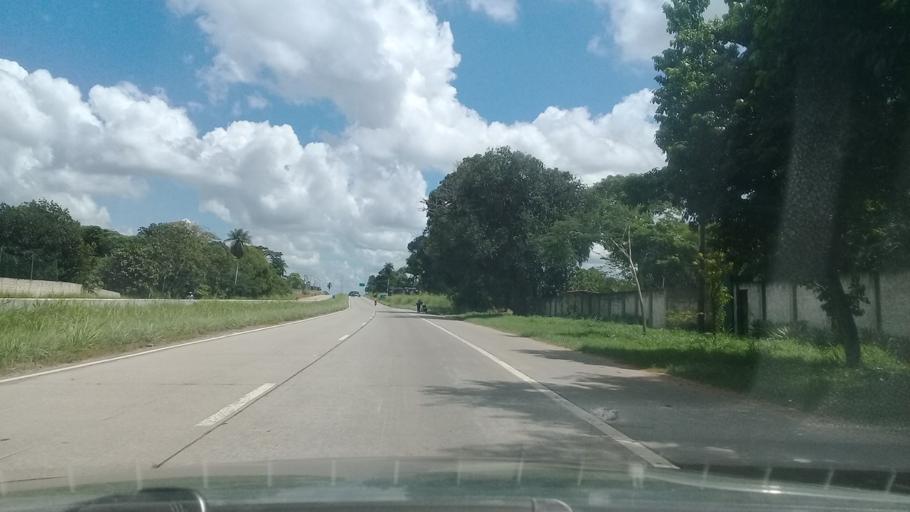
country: BR
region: Pernambuco
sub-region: Carpina
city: Carpina
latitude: -7.9206
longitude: -35.1597
